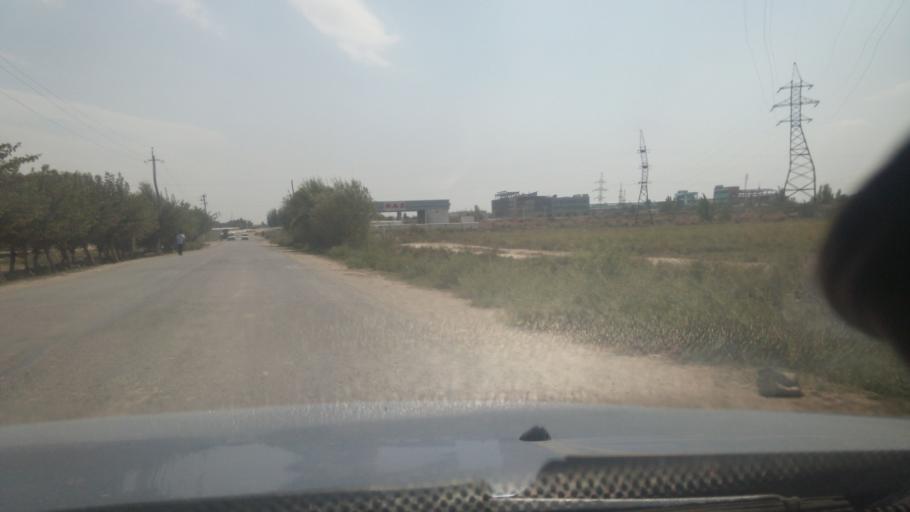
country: UZ
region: Sirdaryo
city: Guliston
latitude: 40.5249
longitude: 68.7684
